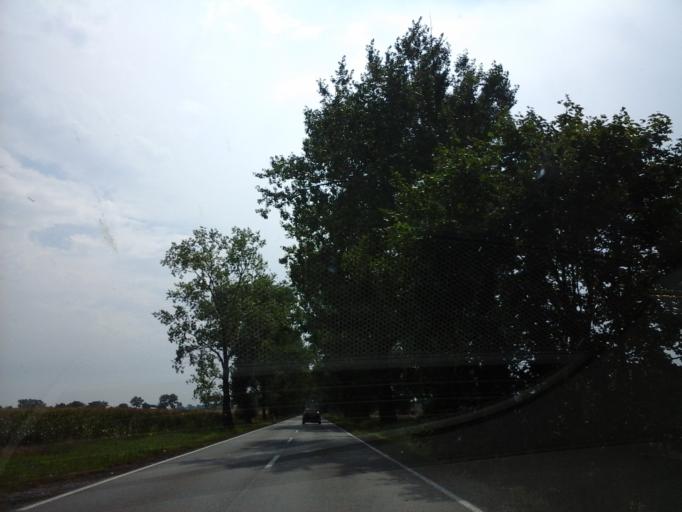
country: PL
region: Lower Silesian Voivodeship
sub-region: Powiat strzelinski
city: Strzelin
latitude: 50.8370
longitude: 17.0564
